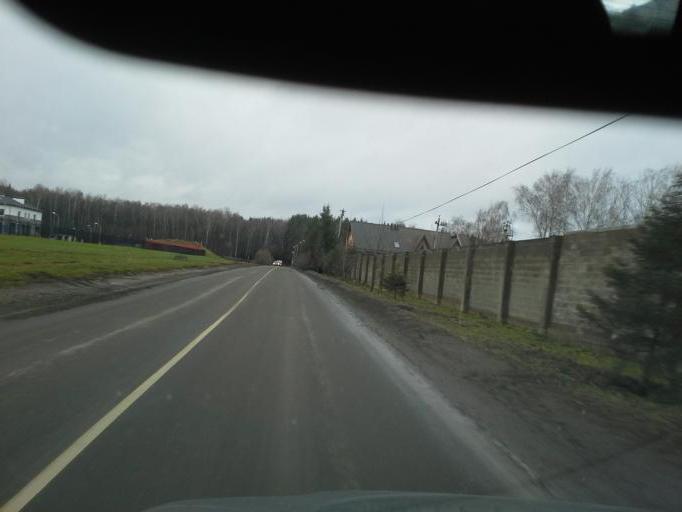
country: RU
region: Moskovskaya
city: Moskovskiy
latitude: 55.5740
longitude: 37.3800
